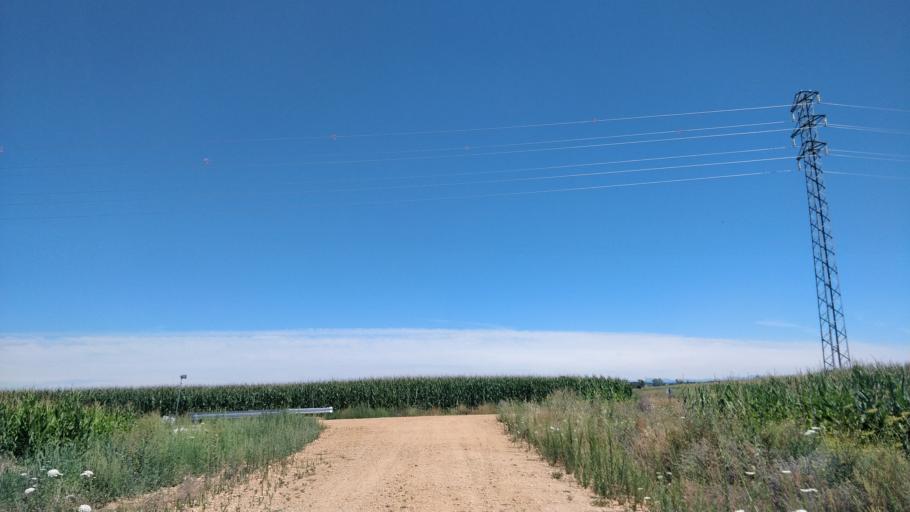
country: ES
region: Castille and Leon
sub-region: Provincia de Leon
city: Bustillo del Paramo
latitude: 42.4600
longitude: -5.8166
